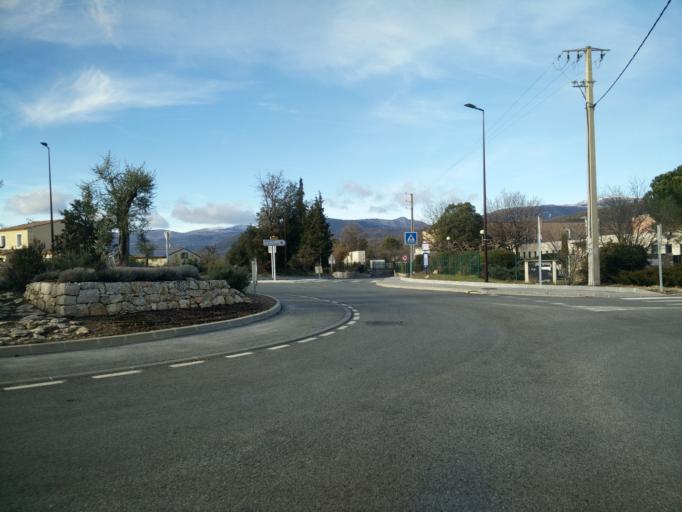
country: FR
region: Provence-Alpes-Cote d'Azur
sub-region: Departement des Alpes-Maritimes
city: Saint-Cezaire-sur-Siagne
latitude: 43.6504
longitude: 6.8164
